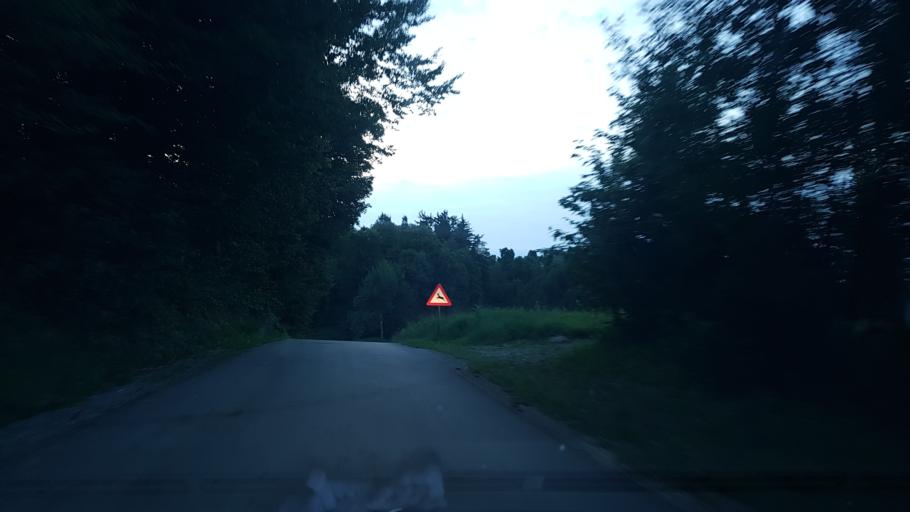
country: SI
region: Postojna
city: Postojna
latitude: 45.7445
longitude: 14.1827
